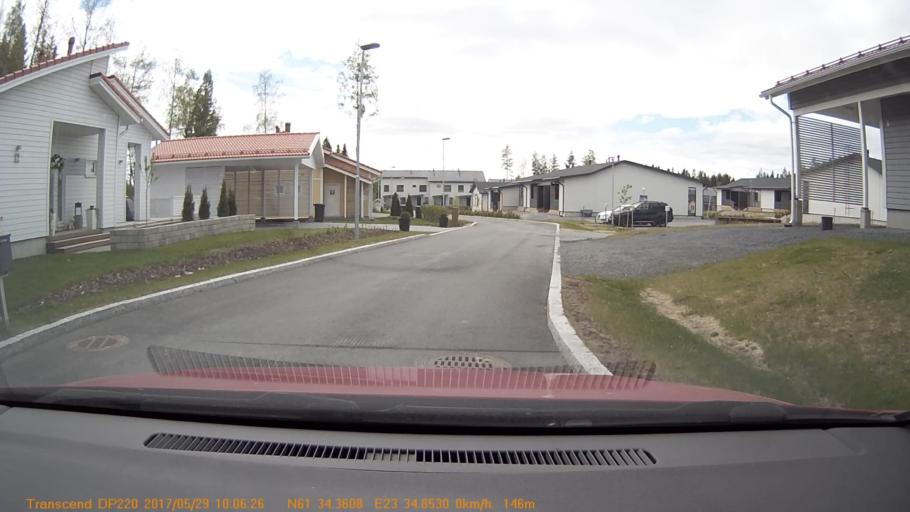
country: FI
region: Pirkanmaa
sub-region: Tampere
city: Yloejaervi
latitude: 61.5727
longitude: 23.5809
